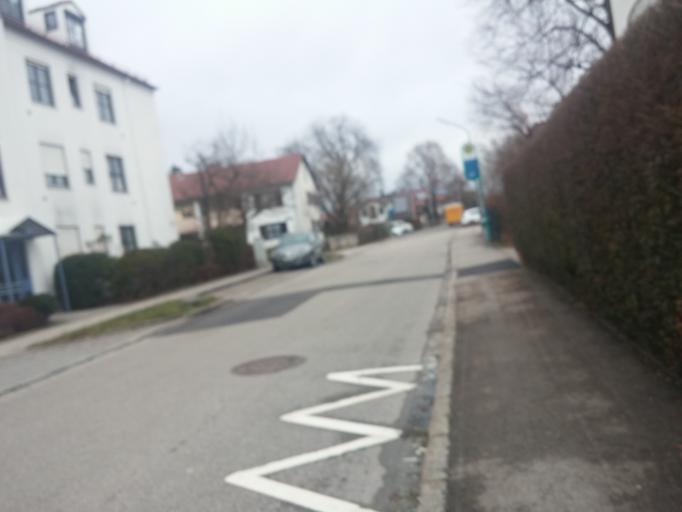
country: DE
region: Bavaria
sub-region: Upper Bavaria
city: Taufkirchen
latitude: 48.0488
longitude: 11.6248
